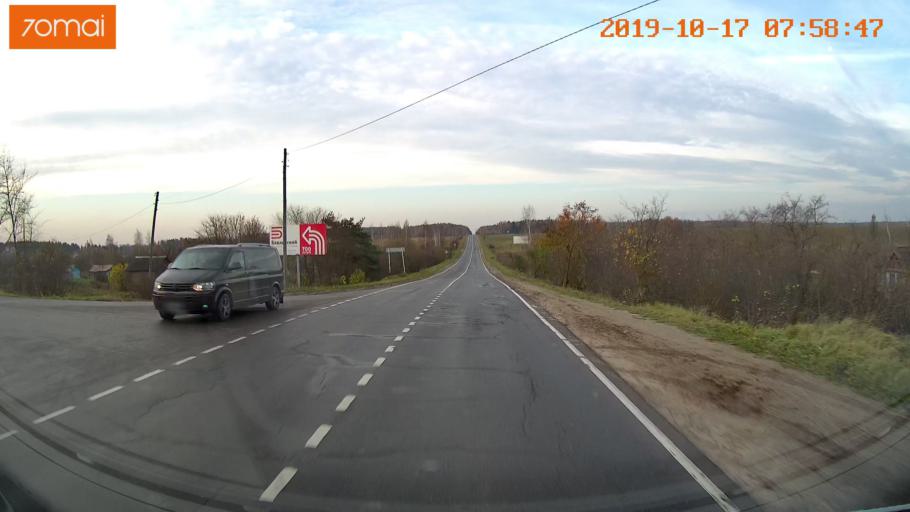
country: RU
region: Vladimir
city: Bavleny
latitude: 56.3994
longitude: 39.5507
